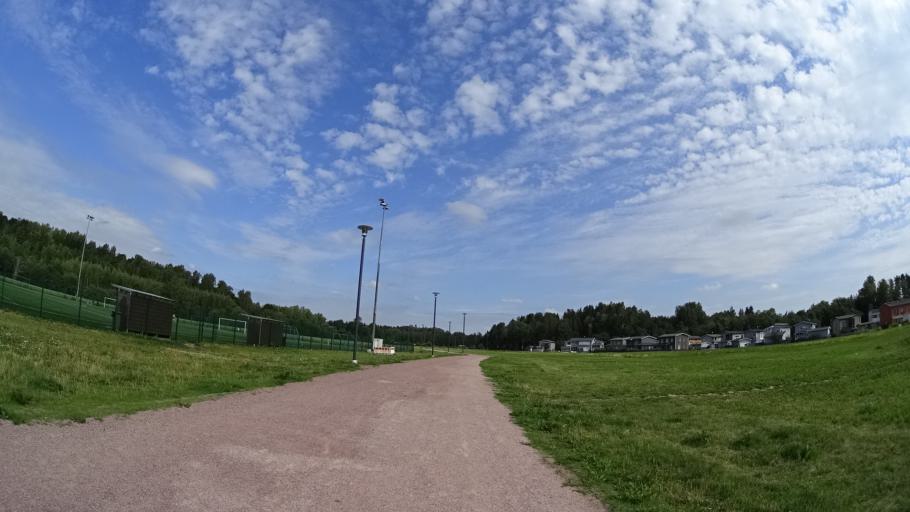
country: FI
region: Uusimaa
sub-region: Helsinki
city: Espoo
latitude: 60.1916
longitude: 24.5858
